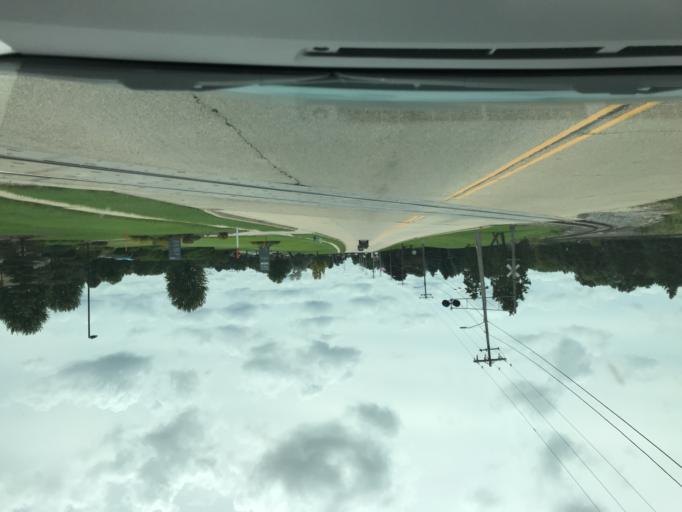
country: US
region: Wisconsin
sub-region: Racine County
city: Burlington
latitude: 42.6681
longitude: -88.2669
